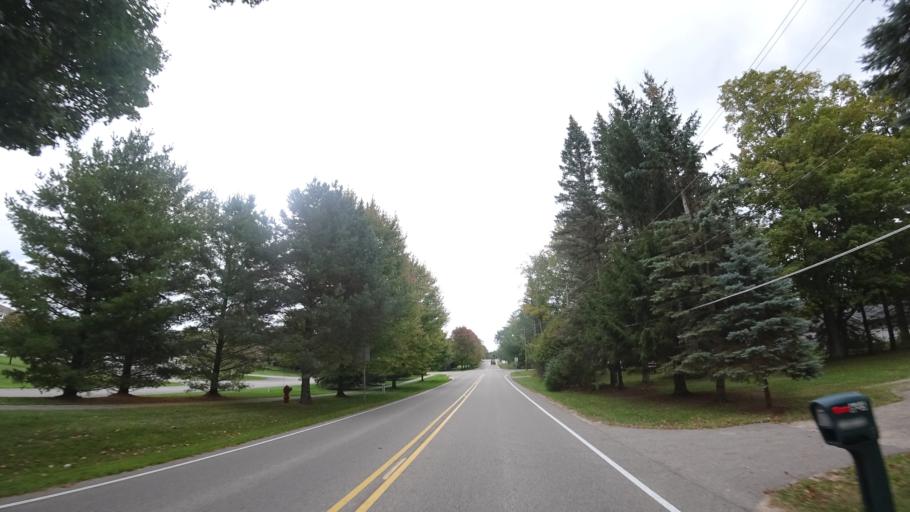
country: US
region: Michigan
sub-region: Emmet County
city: Harbor Springs
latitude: 45.4352
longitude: -84.9997
